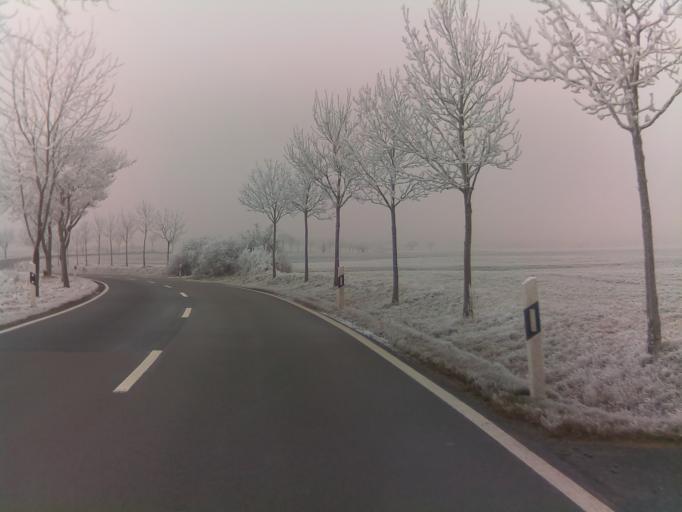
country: DE
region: Thuringia
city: Henneberg
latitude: 50.5162
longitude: 10.3122
